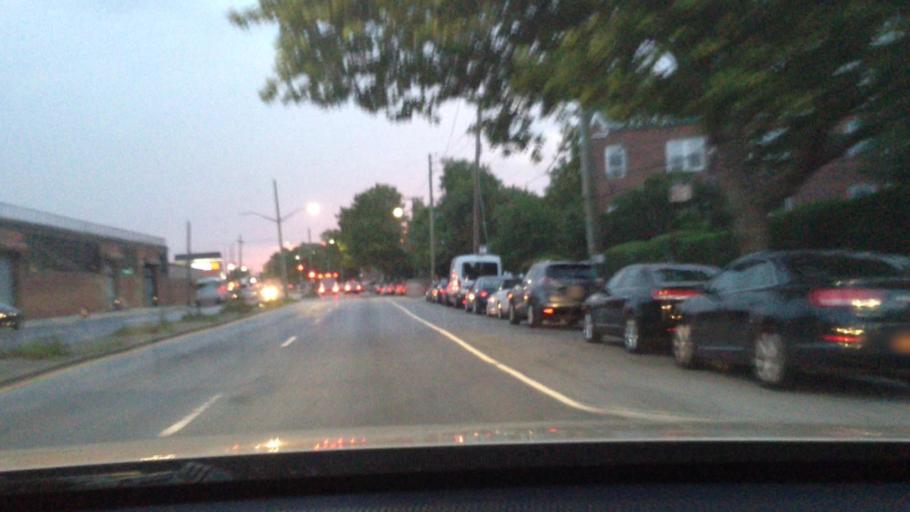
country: US
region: New York
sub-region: Kings County
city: Brooklyn
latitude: 40.6370
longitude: -73.9249
